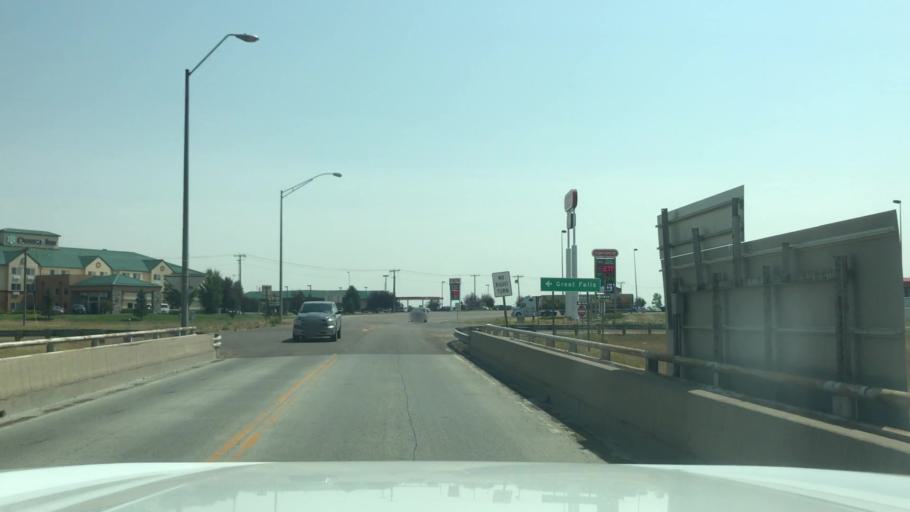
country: US
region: Montana
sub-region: Cascade County
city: Great Falls
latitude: 47.4722
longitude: -111.3609
